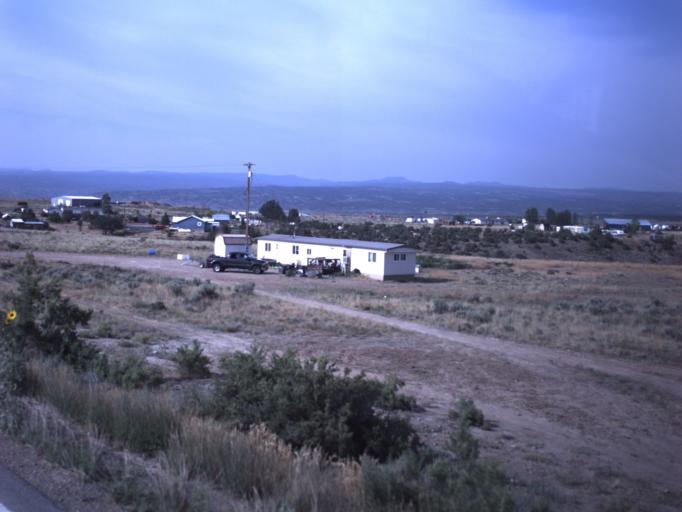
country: US
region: Utah
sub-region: Duchesne County
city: Duchesne
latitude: 40.2053
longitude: -110.3893
